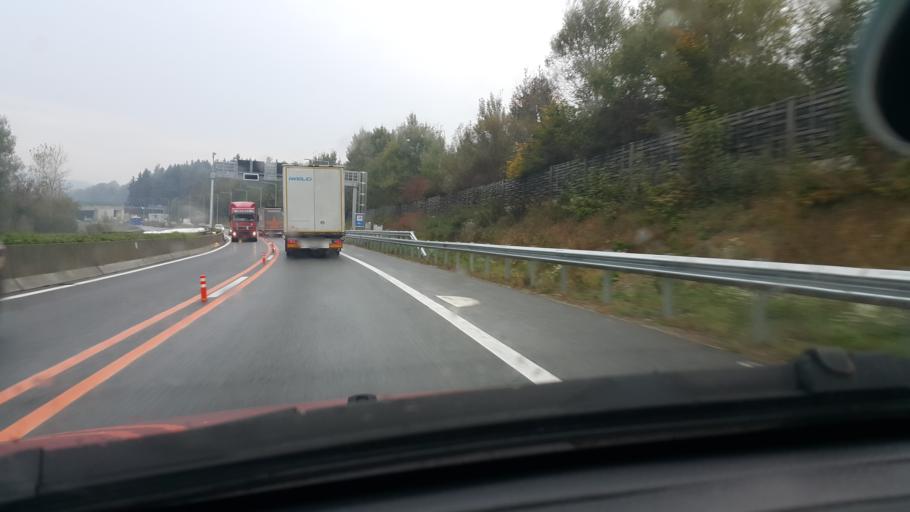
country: AT
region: Carinthia
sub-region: Politischer Bezirk Klagenfurt Land
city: Poggersdorf
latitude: 46.6529
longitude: 14.5370
